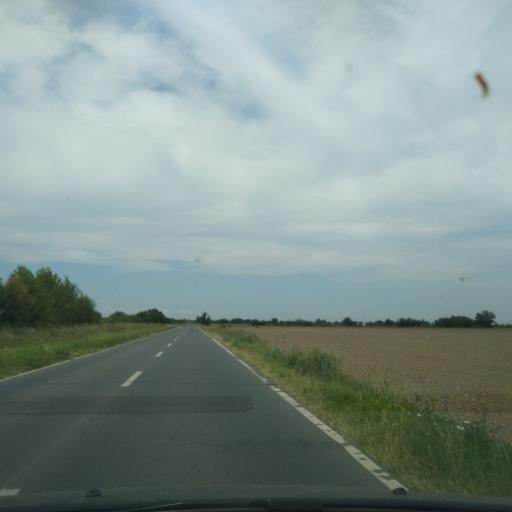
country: RO
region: Ilfov
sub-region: Comuna Tunari
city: Tunari
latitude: 44.5744
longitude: 26.1400
